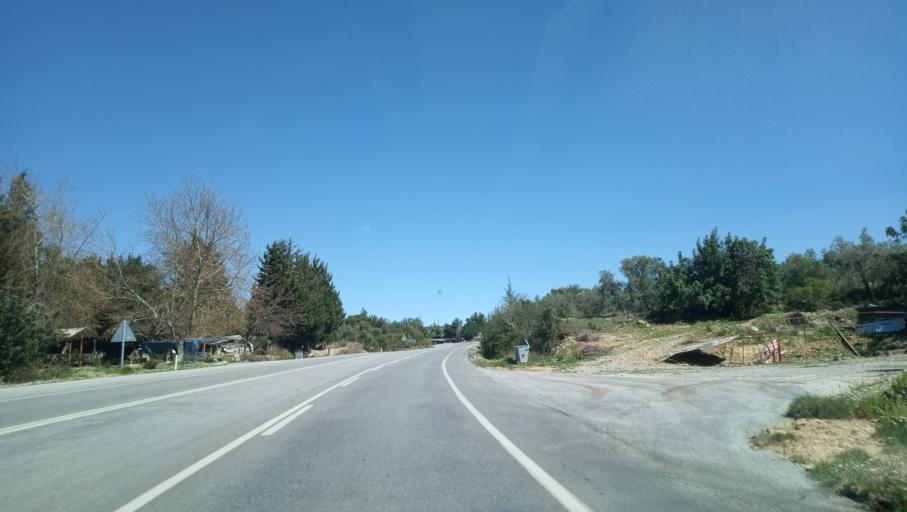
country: TR
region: Antalya
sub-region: Manavgat
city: Kizilagac
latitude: 36.7588
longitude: 31.6360
